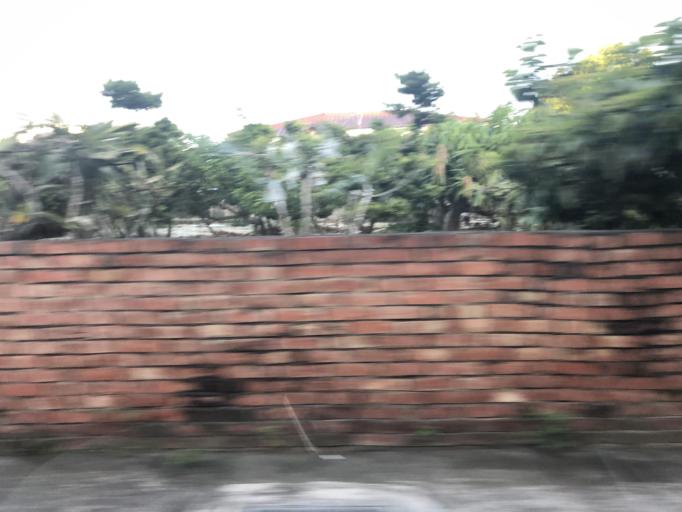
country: TW
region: Taiwan
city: Xinying
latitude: 23.1474
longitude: 120.2722
